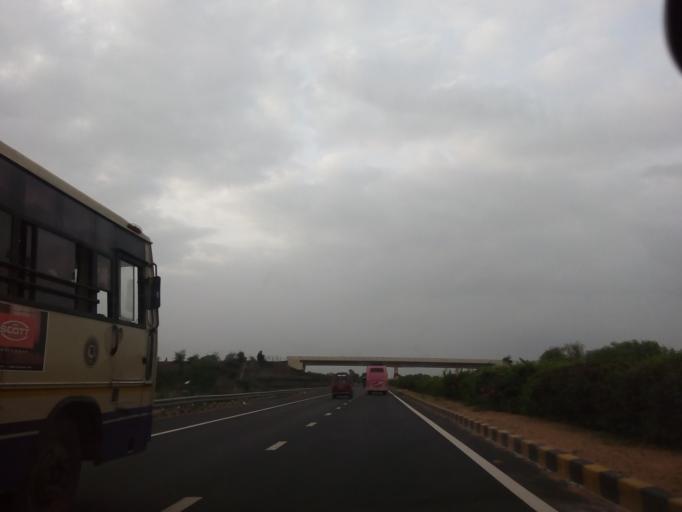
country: IN
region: Gujarat
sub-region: Kheda
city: Mahemdavad
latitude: 22.8944
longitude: 72.7819
